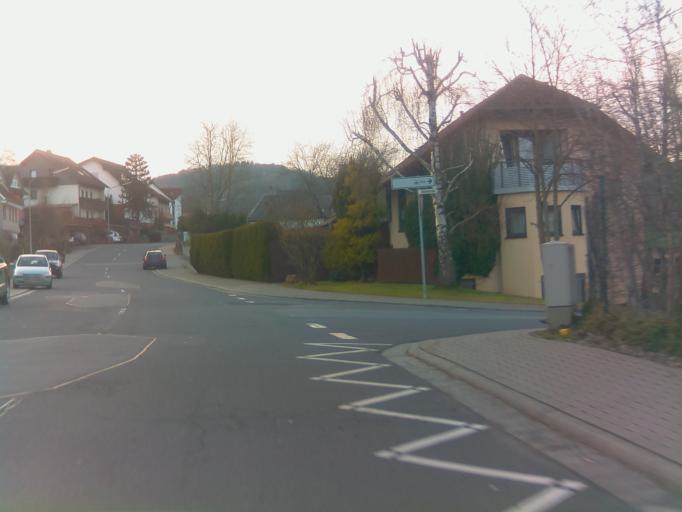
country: DE
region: Hesse
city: Reichelsheim
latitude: 49.7083
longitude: 8.8420
